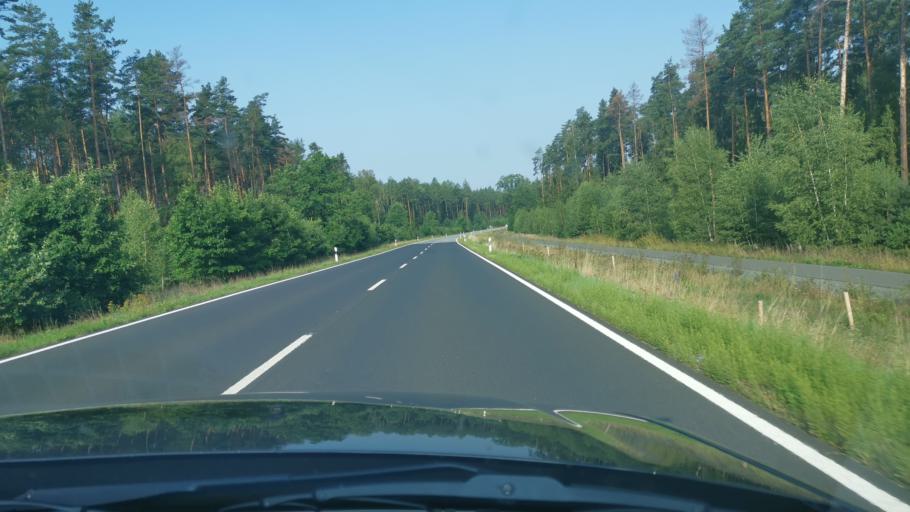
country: DE
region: Bavaria
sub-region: Upper Palatinate
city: Schnaittenbach
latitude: 49.5398
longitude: 12.0734
